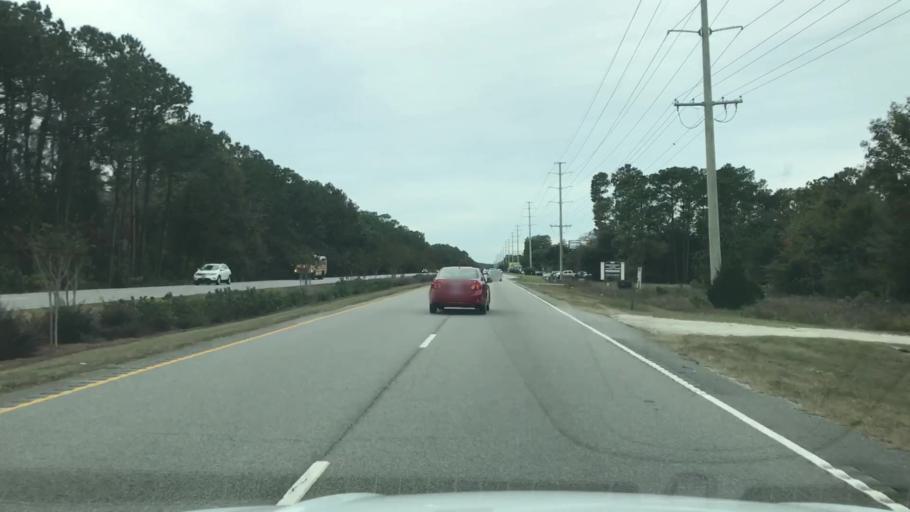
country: US
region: South Carolina
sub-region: Georgetown County
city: Georgetown
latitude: 33.4270
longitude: -79.1537
